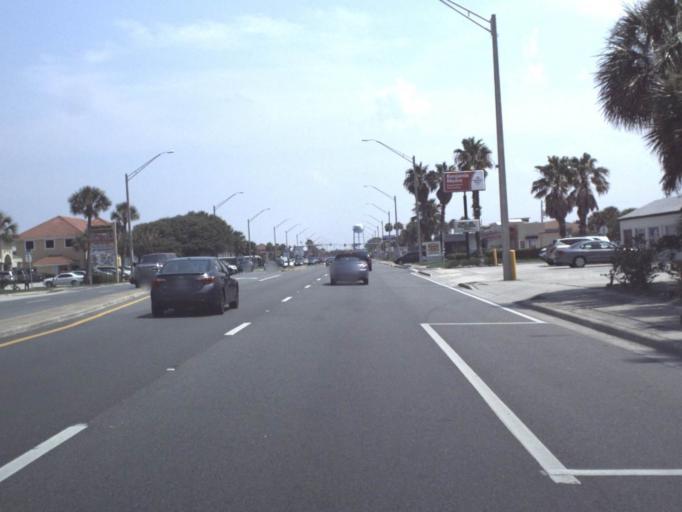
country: US
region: Florida
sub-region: Duval County
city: Jacksonville Beach
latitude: 30.2796
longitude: -81.3901
